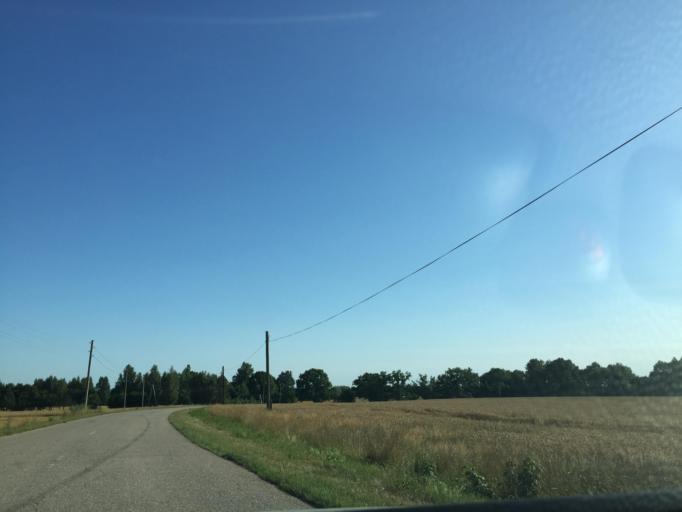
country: LV
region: Talsu Rajons
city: Stende
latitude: 57.1483
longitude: 22.6276
